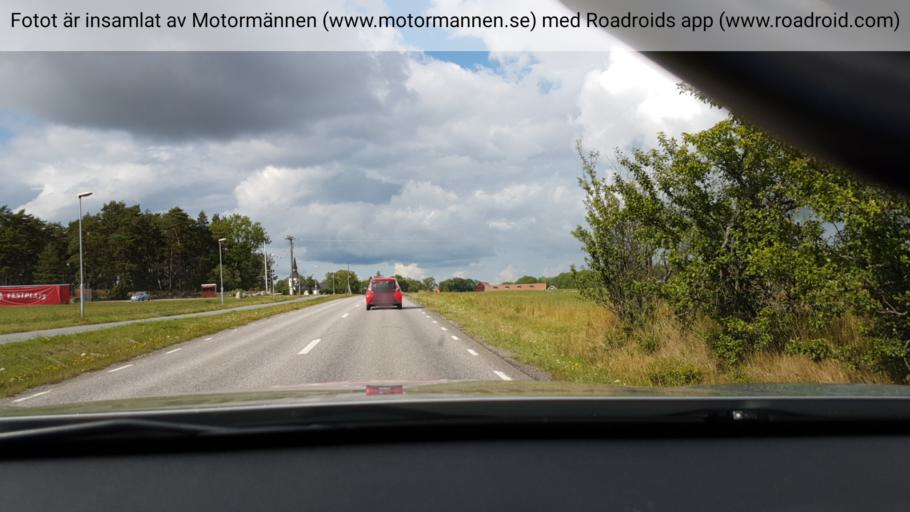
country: SE
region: Stockholm
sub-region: Ekero Kommun
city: Ekeroe
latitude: 59.3272
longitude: 17.7467
